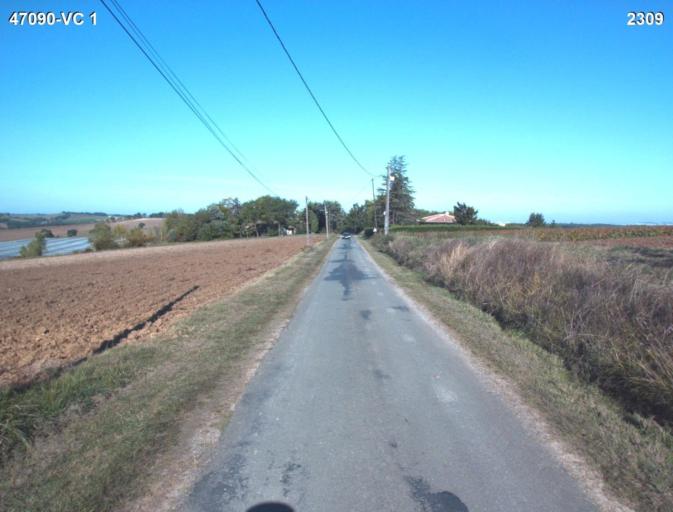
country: FR
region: Aquitaine
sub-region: Departement du Lot-et-Garonne
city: Nerac
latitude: 44.1576
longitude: 0.3927
